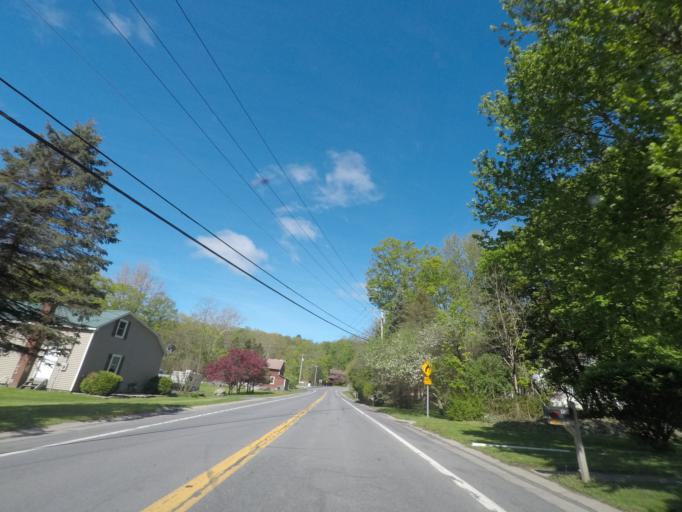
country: US
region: New York
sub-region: Albany County
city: Ravena
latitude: 42.4740
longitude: -73.9211
